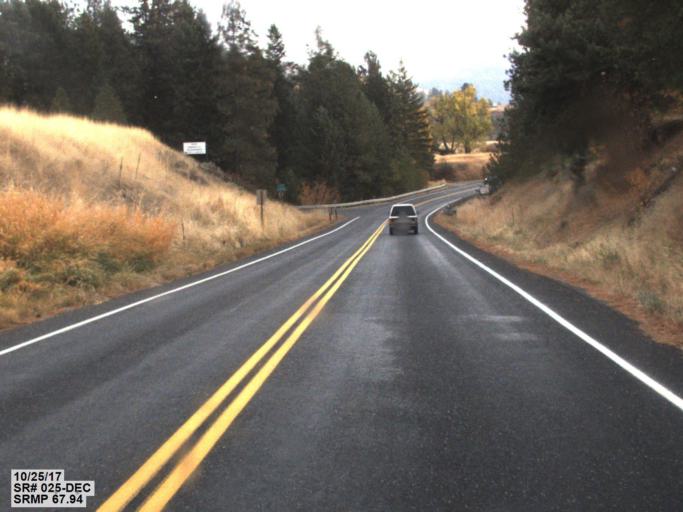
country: US
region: Washington
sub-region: Stevens County
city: Kettle Falls
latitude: 48.4515
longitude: -118.1739
